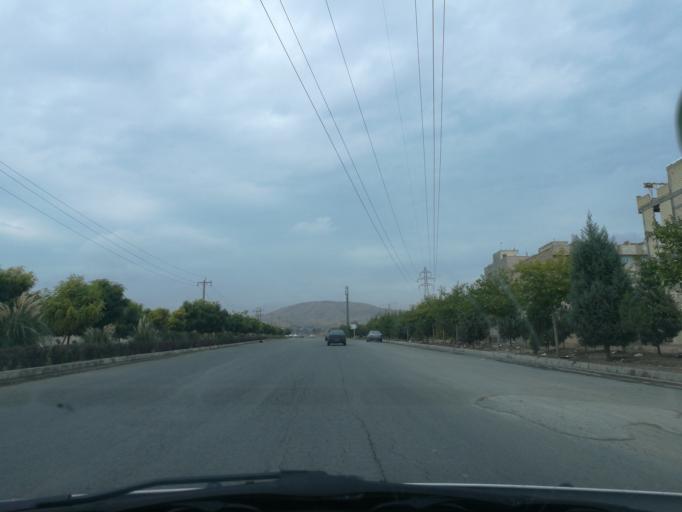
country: IR
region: Alborz
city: Karaj
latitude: 35.8634
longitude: 50.9265
